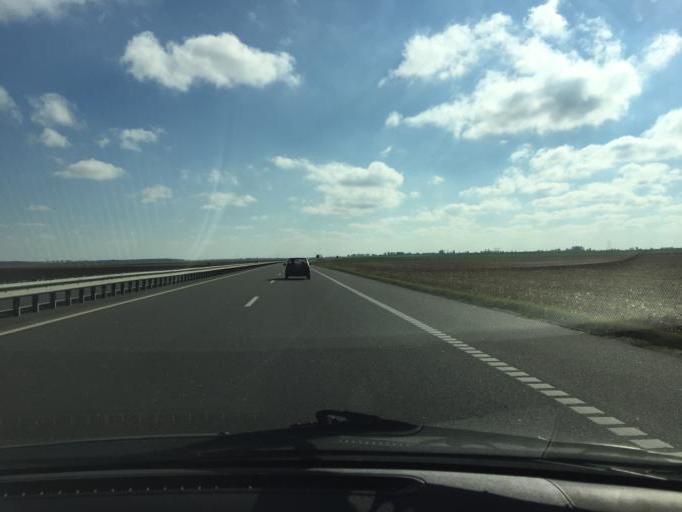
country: BY
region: Minsk
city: Slutsk
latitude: 53.1346
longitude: 27.5554
